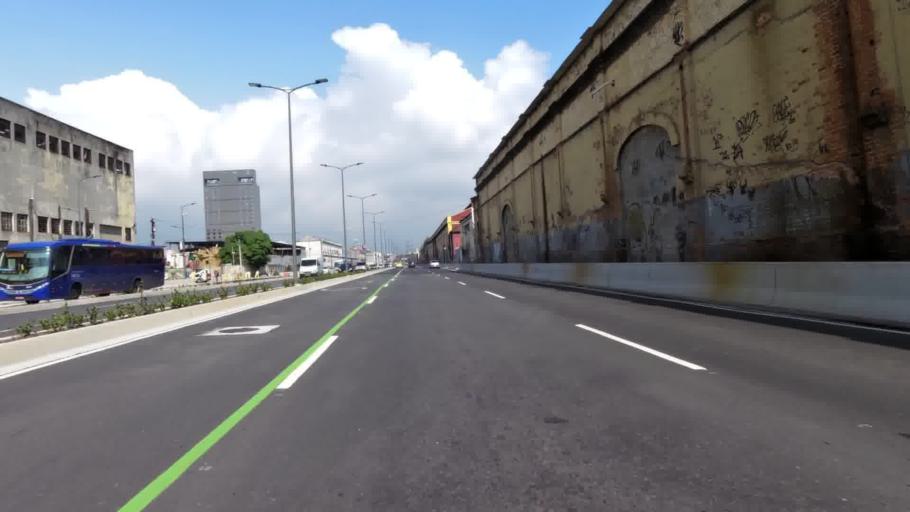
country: BR
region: Rio de Janeiro
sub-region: Rio De Janeiro
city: Rio de Janeiro
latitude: -22.8954
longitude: -43.2026
